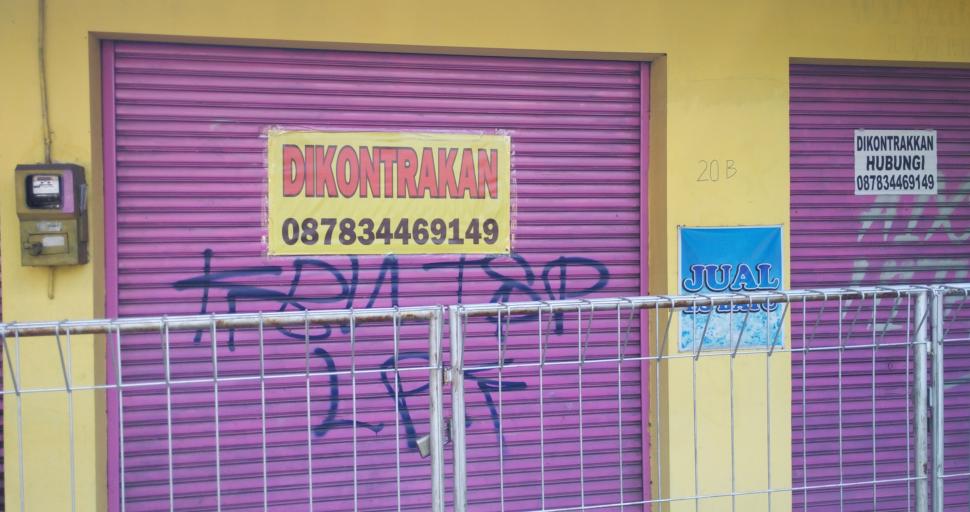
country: ID
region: Daerah Istimewa Yogyakarta
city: Yogyakarta
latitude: -7.8030
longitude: 110.3513
